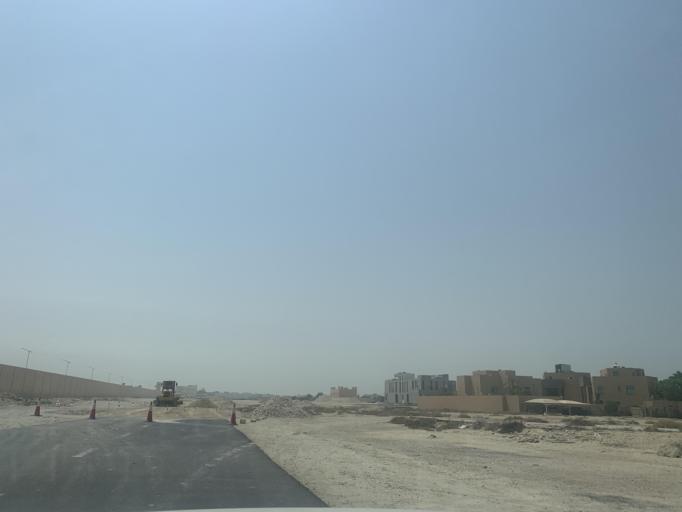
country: BH
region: Central Governorate
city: Madinat Hamad
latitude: 26.1477
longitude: 50.4778
